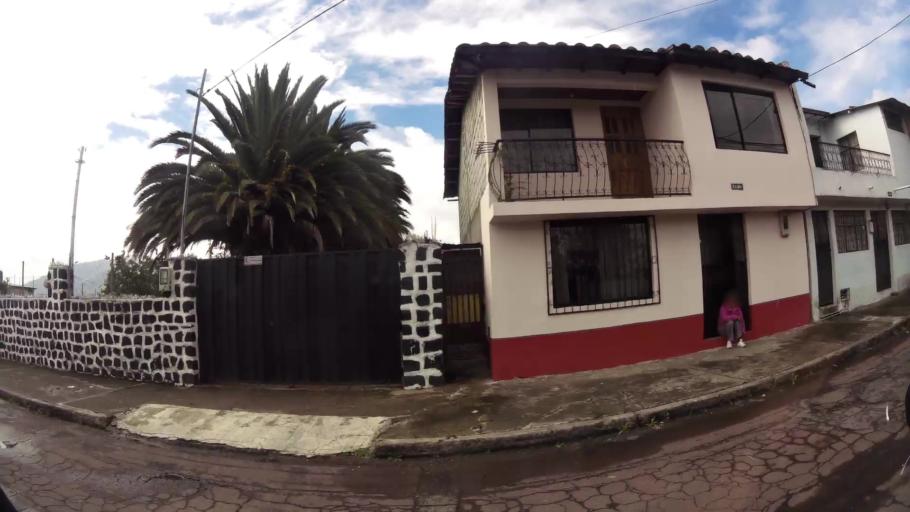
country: EC
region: Pichincha
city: Sangolqui
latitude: -0.3090
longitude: -78.4132
